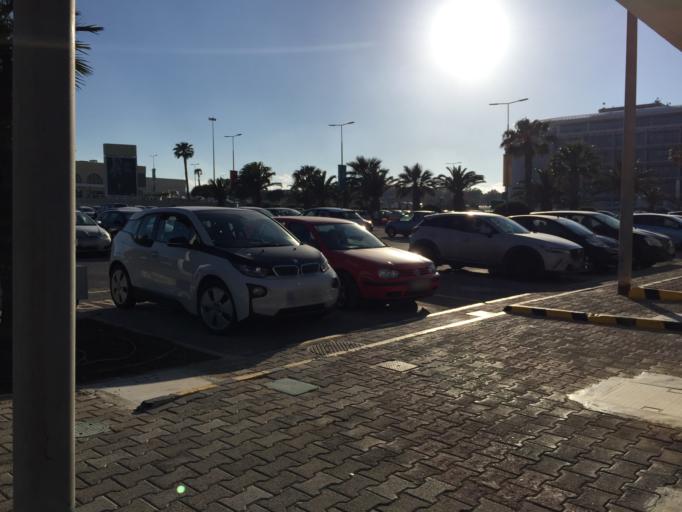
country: MT
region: Il-Gudja
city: Gudja
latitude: 35.8504
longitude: 14.4963
